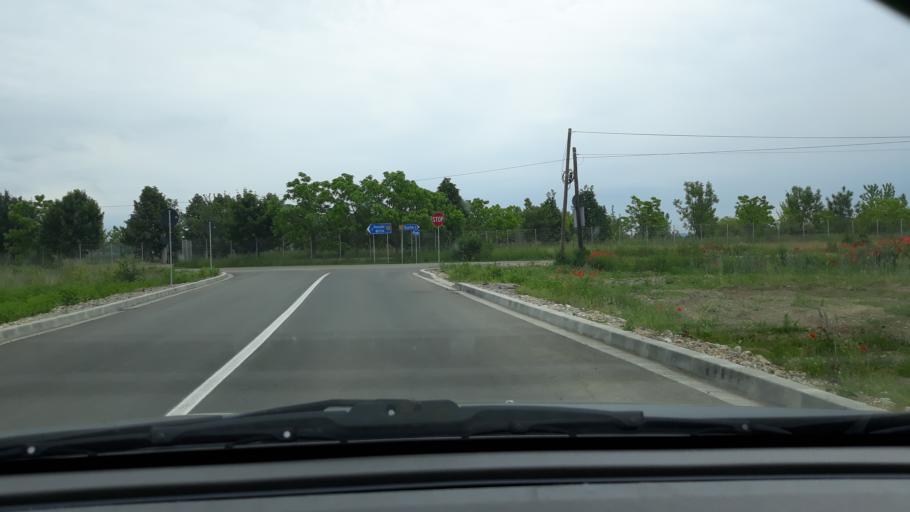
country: RO
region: Bihor
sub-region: Comuna Osorheiu
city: Osorheiu
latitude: 47.0660
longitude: 22.0411
